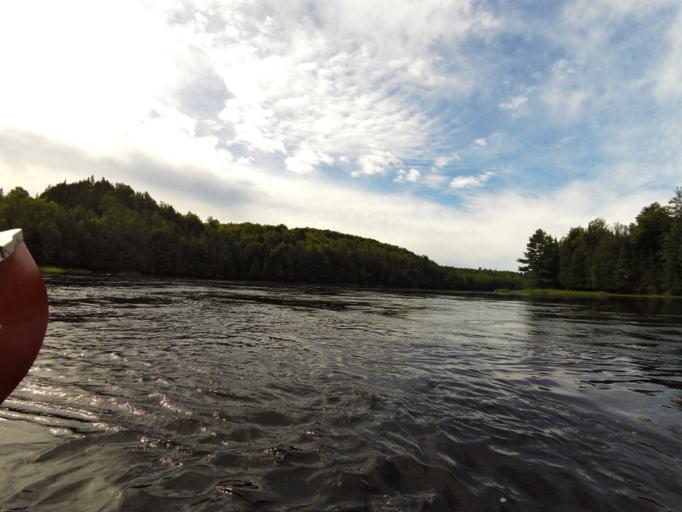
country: CA
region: Quebec
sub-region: Outaouais
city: Wakefield
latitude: 45.7954
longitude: -75.9318
